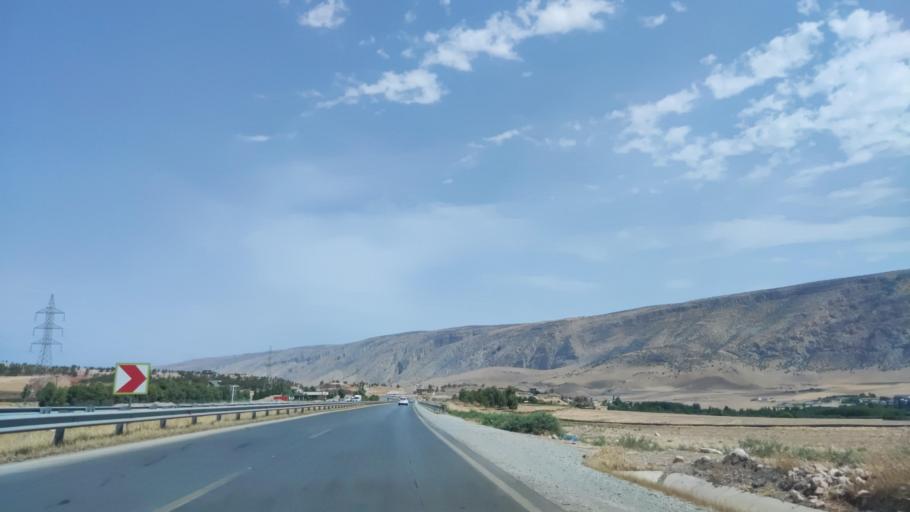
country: IQ
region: Arbil
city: Shaqlawah
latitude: 36.4784
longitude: 44.3806
